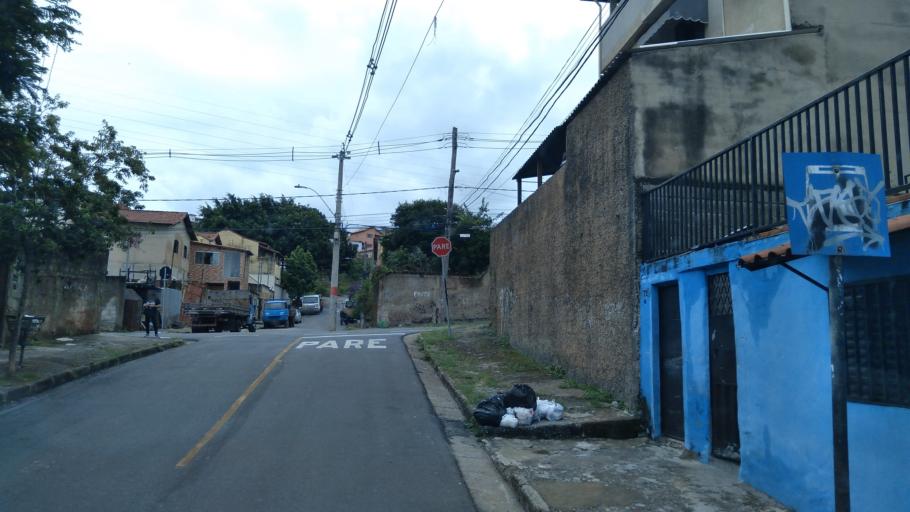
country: BR
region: Minas Gerais
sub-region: Belo Horizonte
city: Belo Horizonte
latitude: -19.8907
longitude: -43.8952
